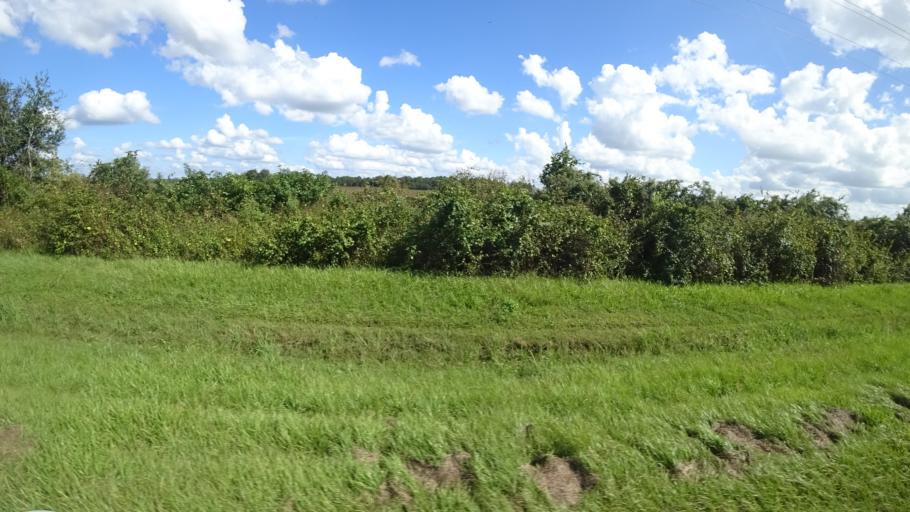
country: US
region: Florida
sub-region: Sarasota County
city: Lake Sarasota
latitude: 27.3770
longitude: -82.1402
